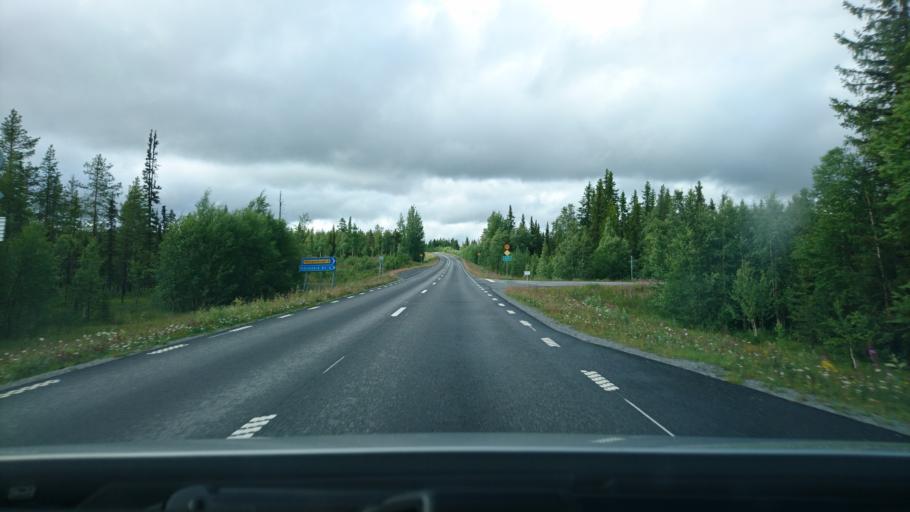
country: SE
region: Vaesterbotten
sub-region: Vilhelmina Kommun
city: Vilhelmina
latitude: 64.7370
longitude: 16.7095
